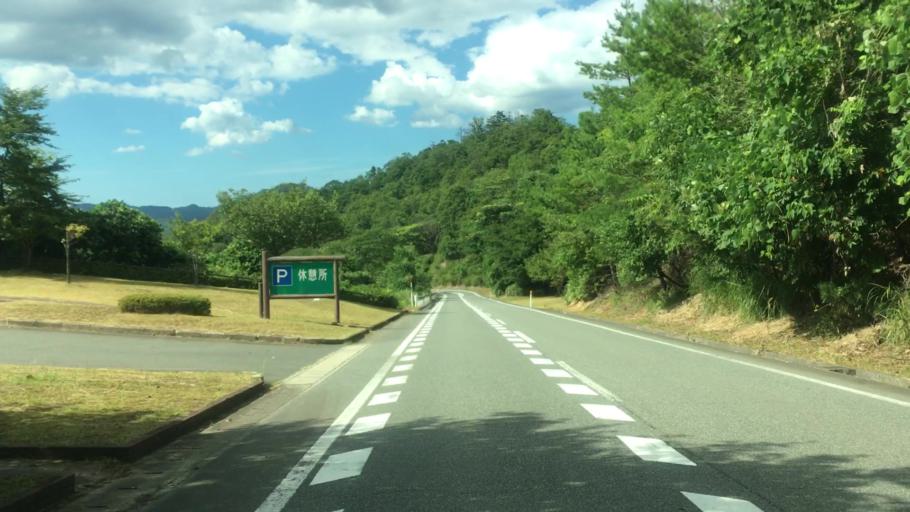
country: JP
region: Hyogo
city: Toyooka
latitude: 35.5220
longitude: 134.7915
